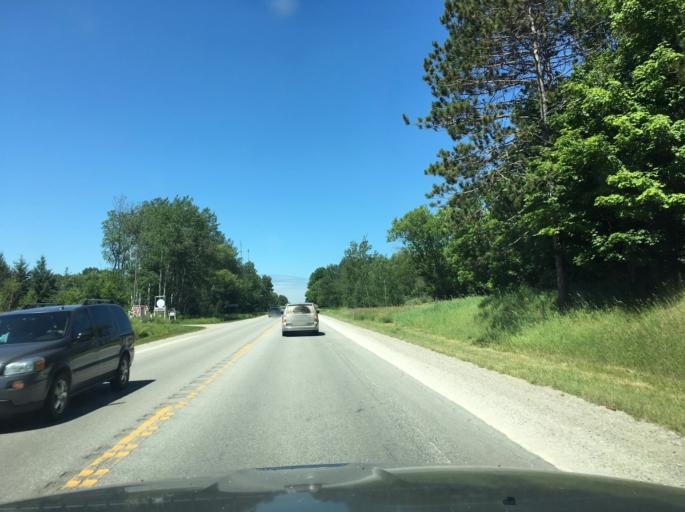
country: US
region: Michigan
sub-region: Osceola County
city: Reed City
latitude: 43.8878
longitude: -85.5838
